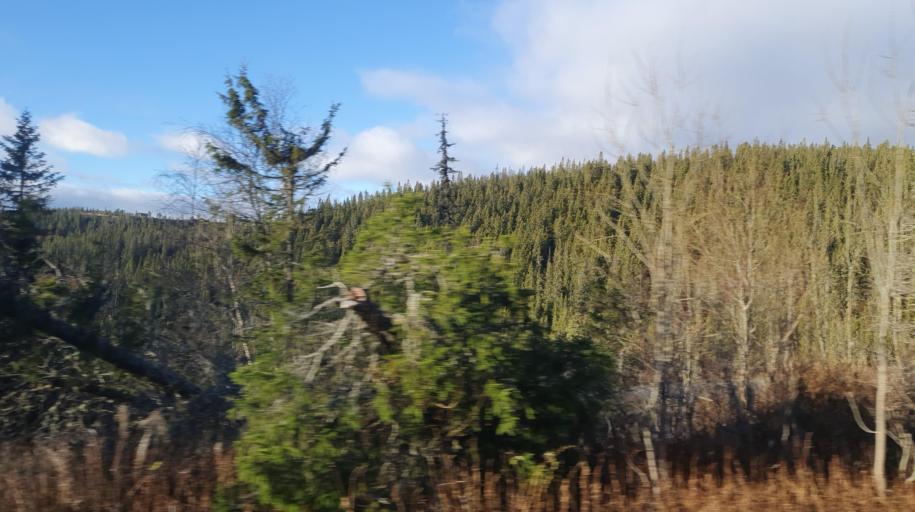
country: NO
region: Buskerud
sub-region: Krodsherad
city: Noresund
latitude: 60.2205
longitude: 9.5334
